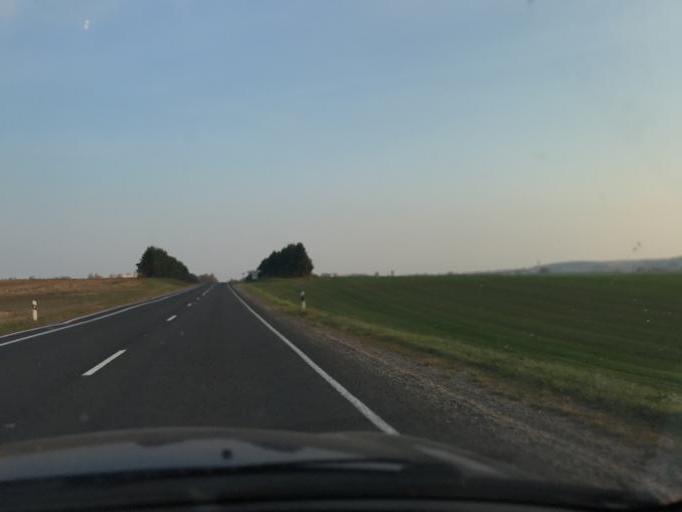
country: BY
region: Grodnenskaya
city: Karelichy
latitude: 53.5815
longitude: 26.1194
